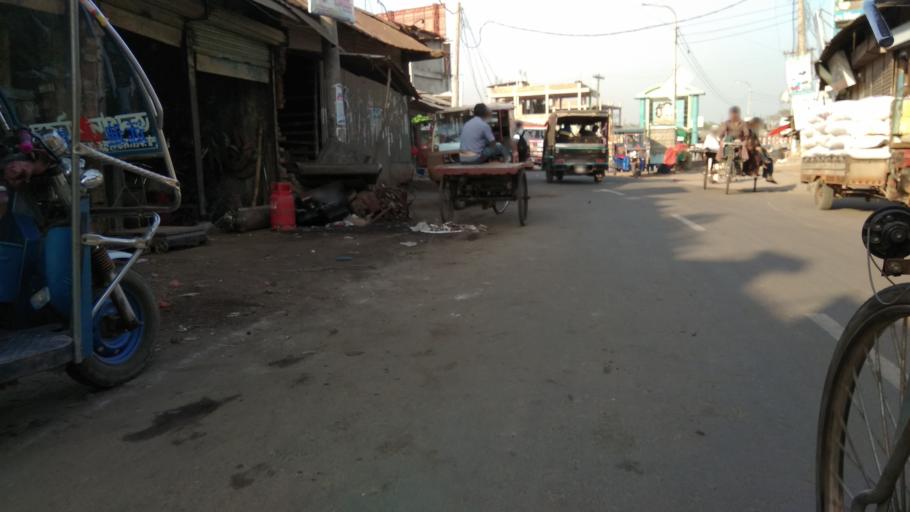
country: BD
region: Barisal
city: Mehendiganj
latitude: 22.9158
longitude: 90.4141
